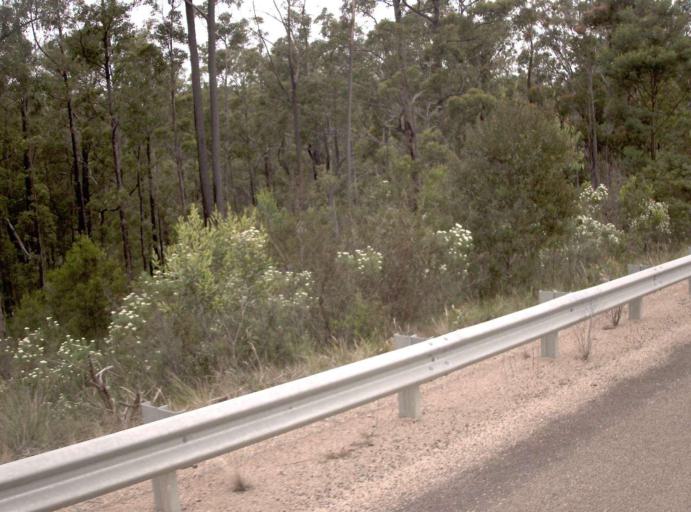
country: AU
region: Victoria
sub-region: East Gippsland
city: Lakes Entrance
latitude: -37.6969
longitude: 148.0482
